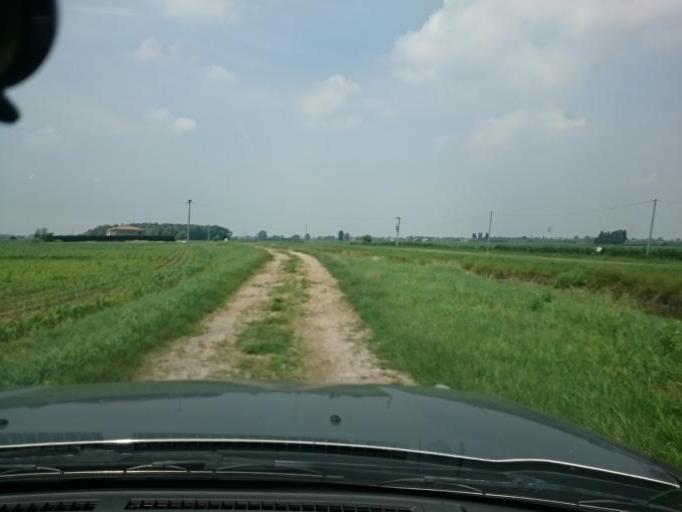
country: IT
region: Veneto
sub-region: Provincia di Padova
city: Correzzola
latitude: 45.2549
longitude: 12.0633
